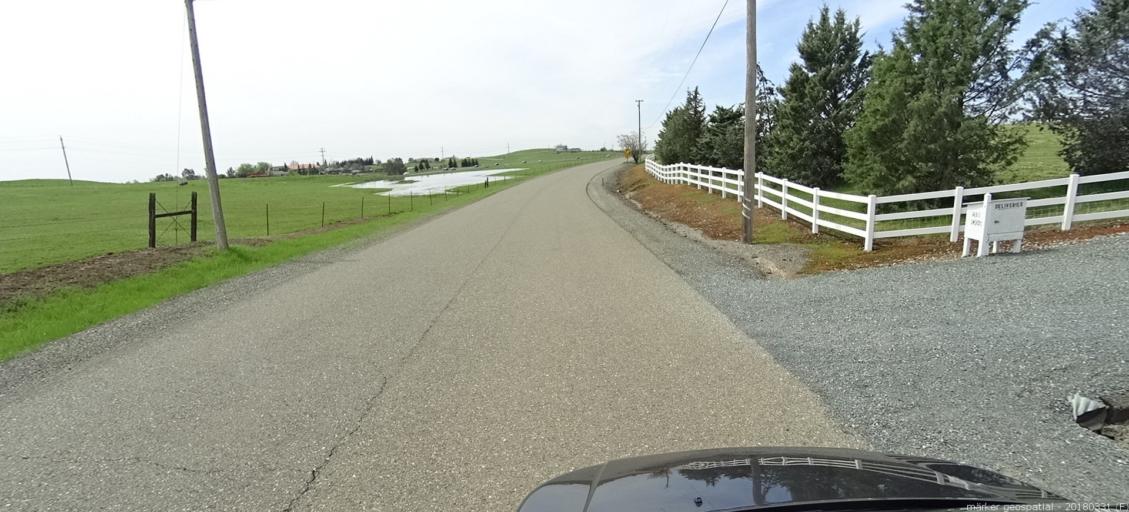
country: US
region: California
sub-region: Sacramento County
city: Rancho Murieta
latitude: 38.4978
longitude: -121.1265
